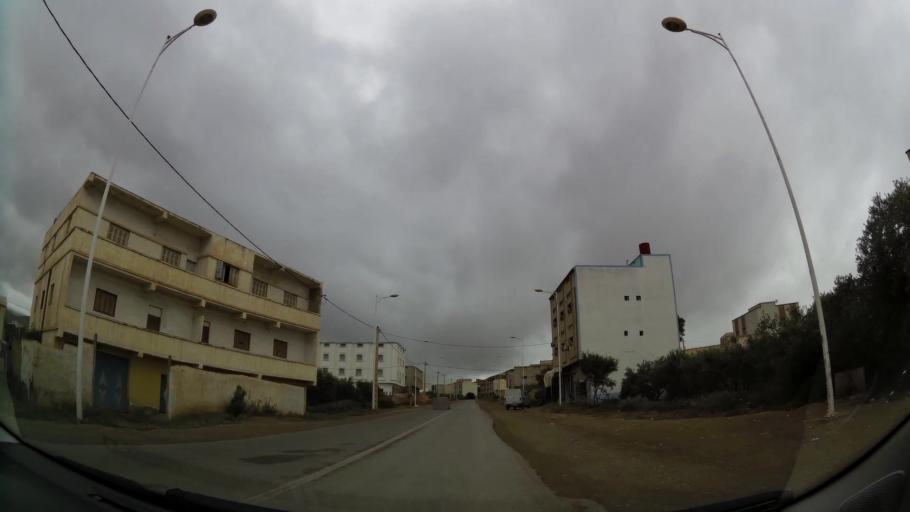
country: MA
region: Oriental
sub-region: Nador
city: Midar
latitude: 35.0554
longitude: -3.4631
